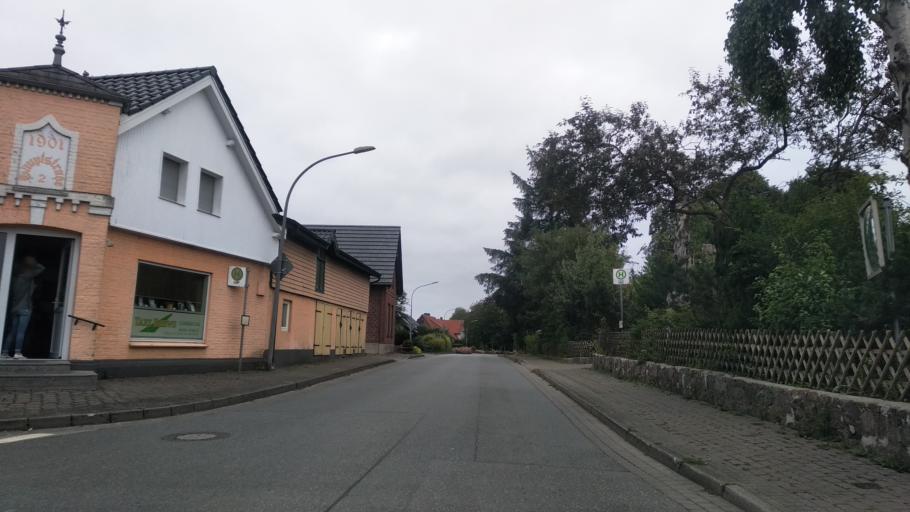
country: DE
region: Schleswig-Holstein
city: Langballig
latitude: 54.7974
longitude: 9.6368
